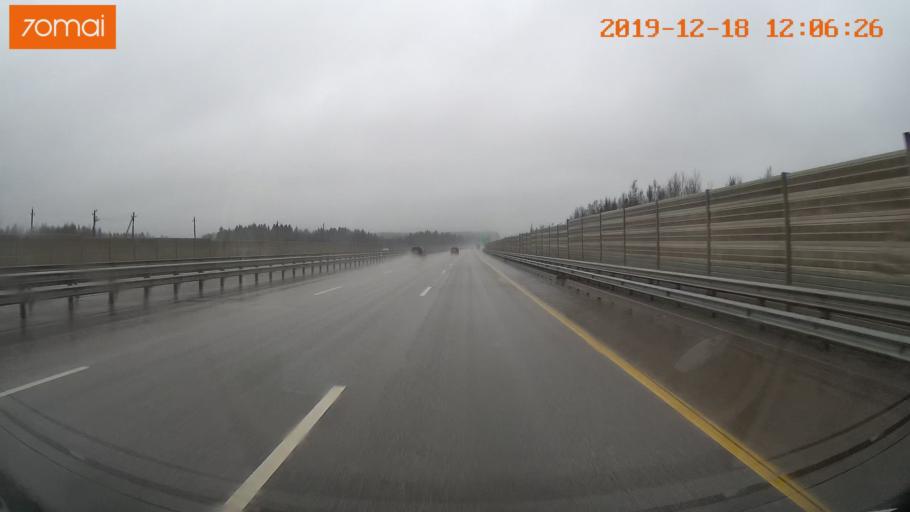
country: RU
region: Moskovskaya
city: Kostrovo
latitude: 55.8801
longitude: 36.6729
